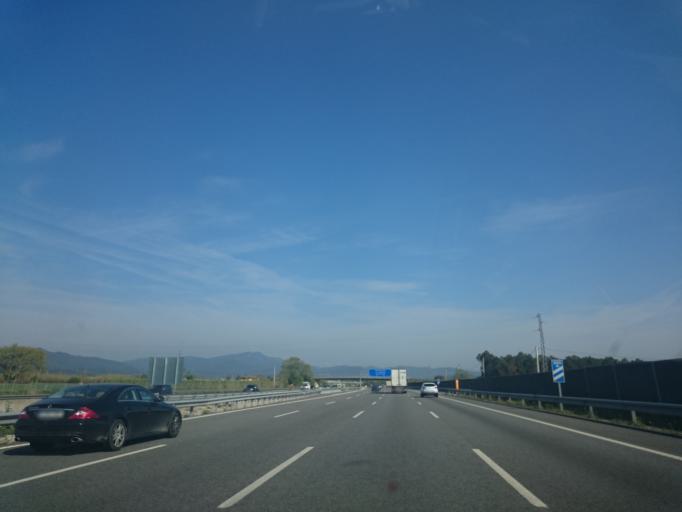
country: ES
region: Catalonia
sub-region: Provincia de Girona
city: Vilablareix
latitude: 41.9530
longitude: 2.7871
